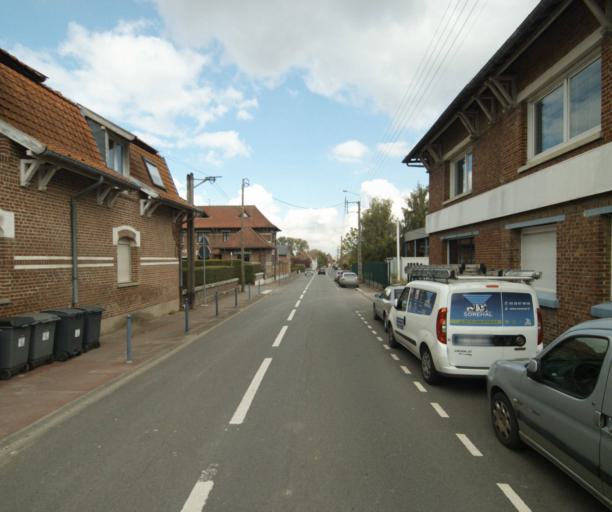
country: FR
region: Nord-Pas-de-Calais
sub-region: Departement du Nord
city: Herlies
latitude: 50.5803
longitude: 2.8527
